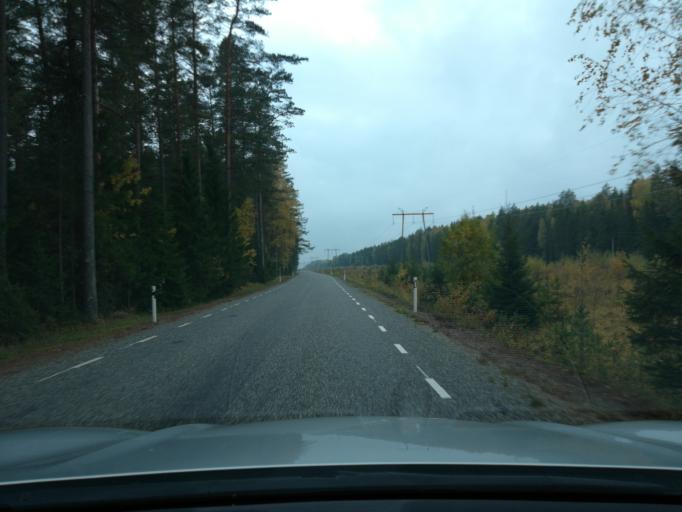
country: EE
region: Ida-Virumaa
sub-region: Johvi vald
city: Johvi
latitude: 59.1637
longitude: 27.4267
